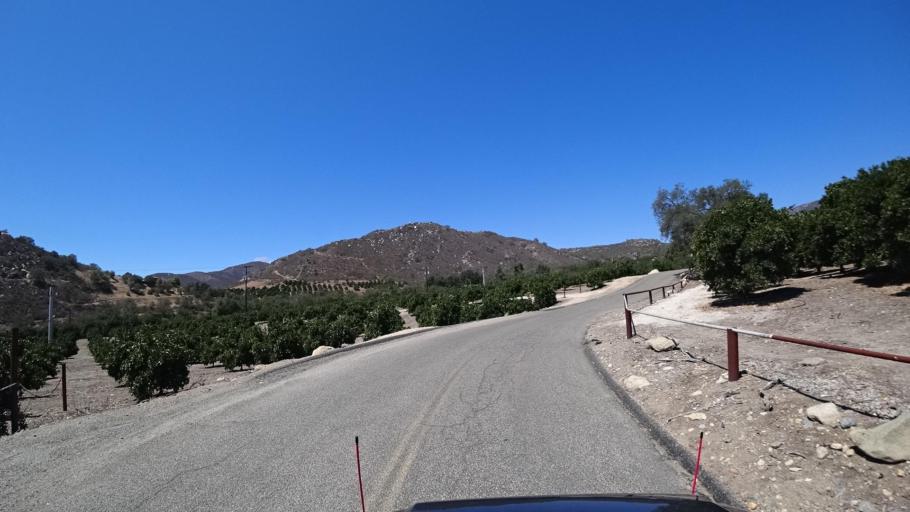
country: US
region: California
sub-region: San Diego County
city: Rainbow
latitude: 33.3807
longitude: -117.0450
